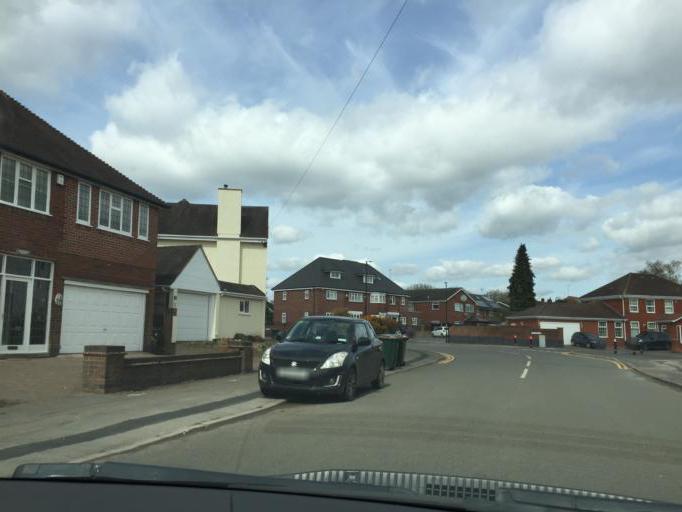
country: GB
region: England
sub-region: Coventry
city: Coventry
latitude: 52.3894
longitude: -1.5147
